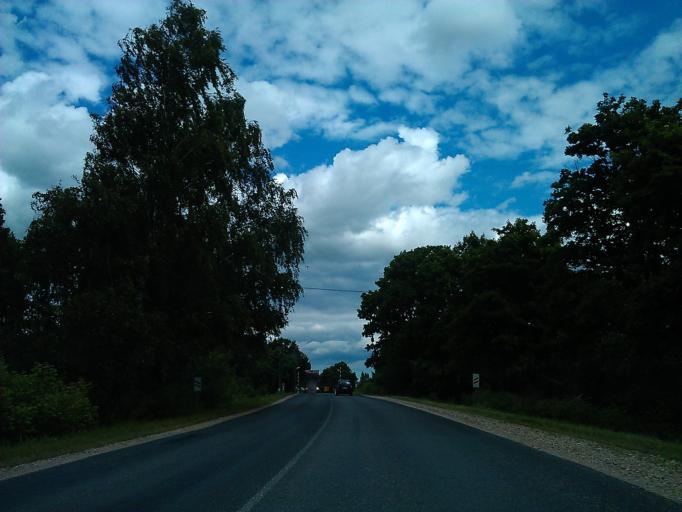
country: LV
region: Jelgava
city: Jelgava
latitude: 56.6449
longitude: 23.6220
